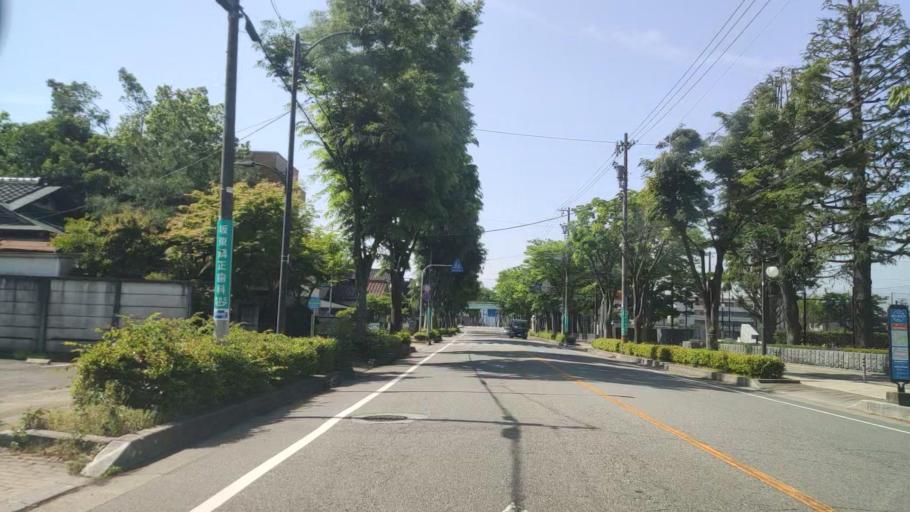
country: JP
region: Toyama
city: Toyama-shi
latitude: 36.6955
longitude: 137.2048
